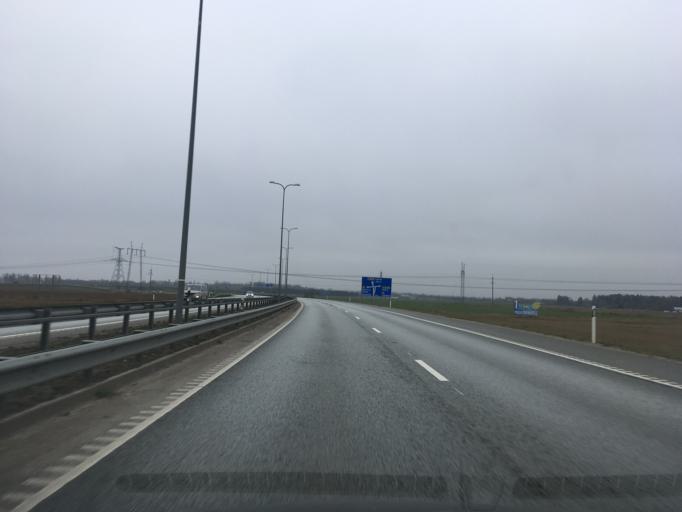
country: EE
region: Ida-Virumaa
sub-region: Kohtla-Jaerve linn
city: Kohtla-Jarve
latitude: 59.3924
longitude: 27.3371
